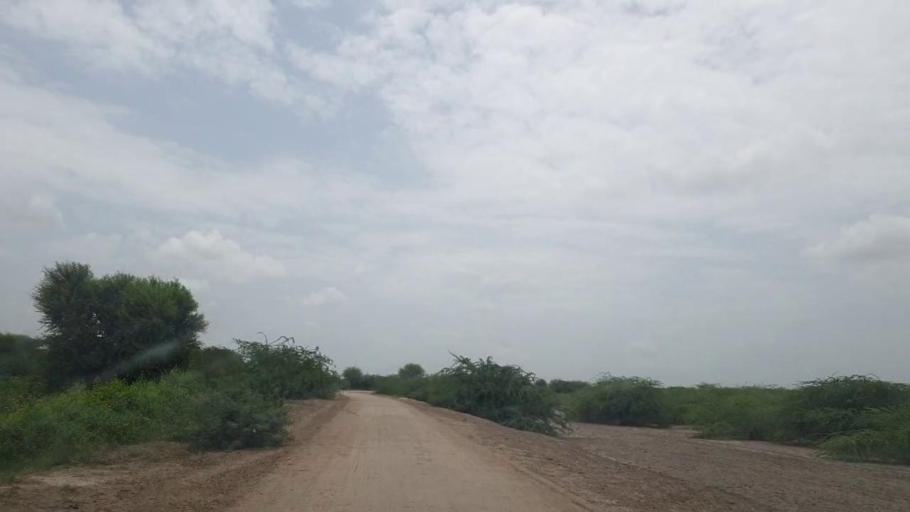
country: PK
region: Sindh
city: Digri
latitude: 24.9321
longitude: 69.1798
